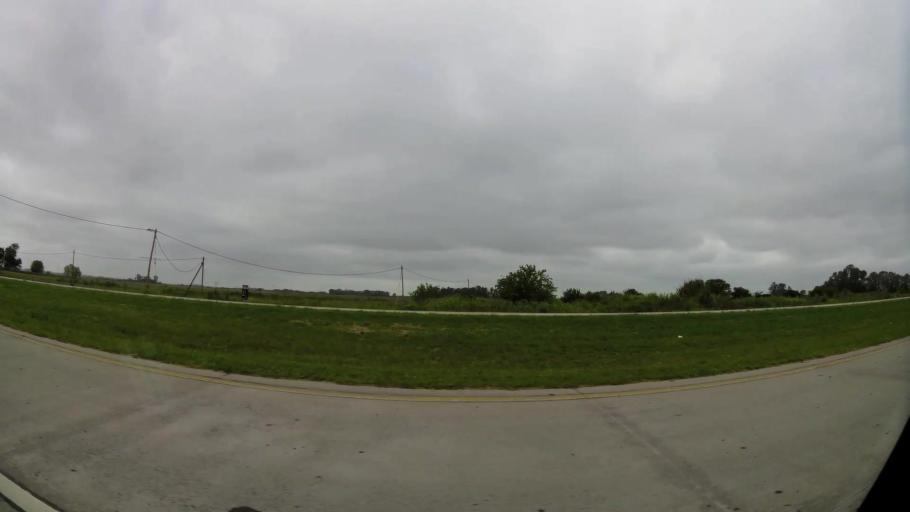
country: AR
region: Buenos Aires
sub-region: Partido de Brandsen
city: Brandsen
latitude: -35.0318
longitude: -58.2014
